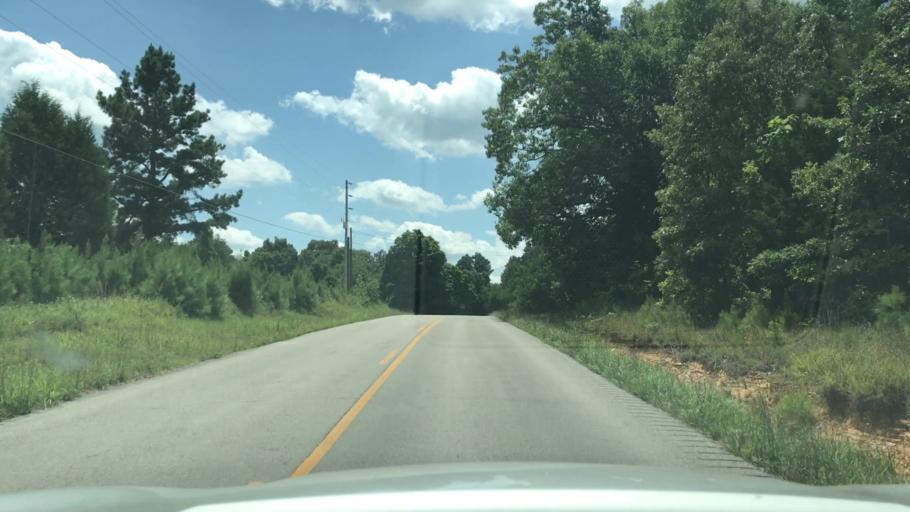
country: US
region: Kentucky
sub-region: Hopkins County
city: Nortonville
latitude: 37.1170
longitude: -87.3243
